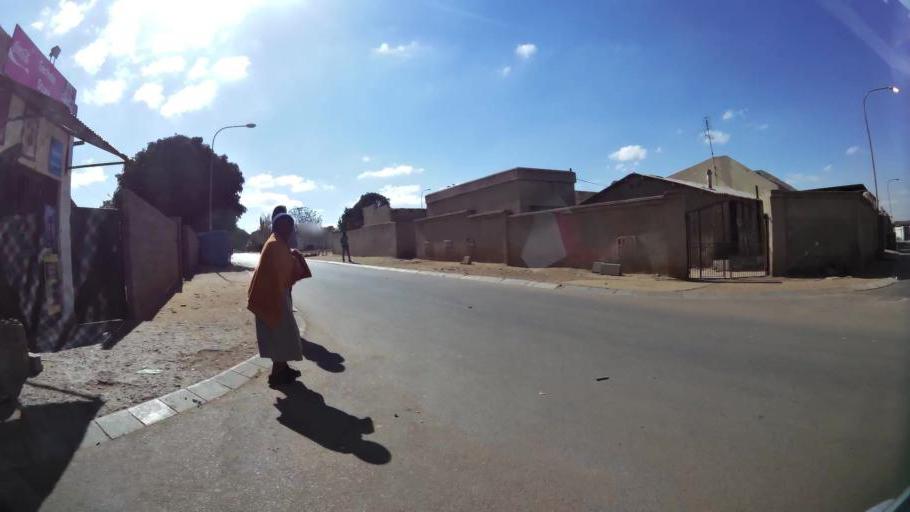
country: ZA
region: Gauteng
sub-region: City of Johannesburg Metropolitan Municipality
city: Roodepoort
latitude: -26.2179
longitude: 27.8954
